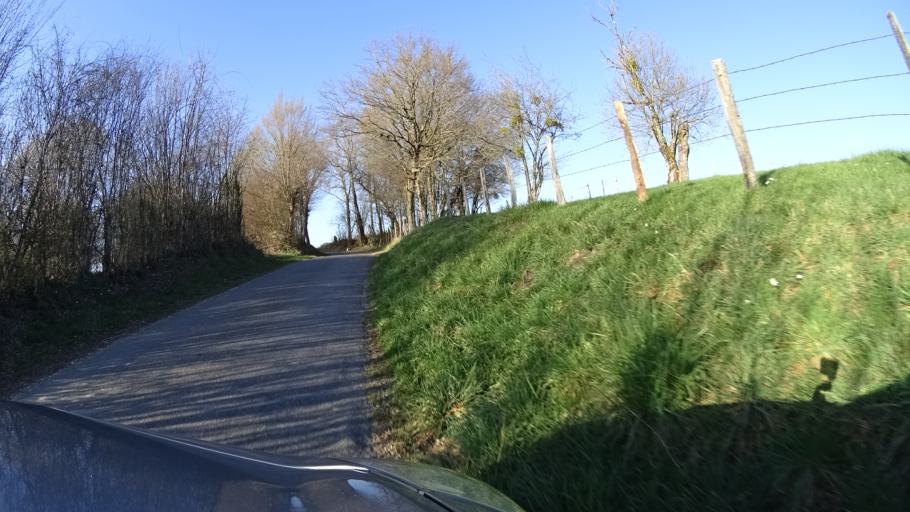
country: FR
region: Franche-Comte
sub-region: Departement du Doubs
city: Morre
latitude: 47.1930
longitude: 6.0541
